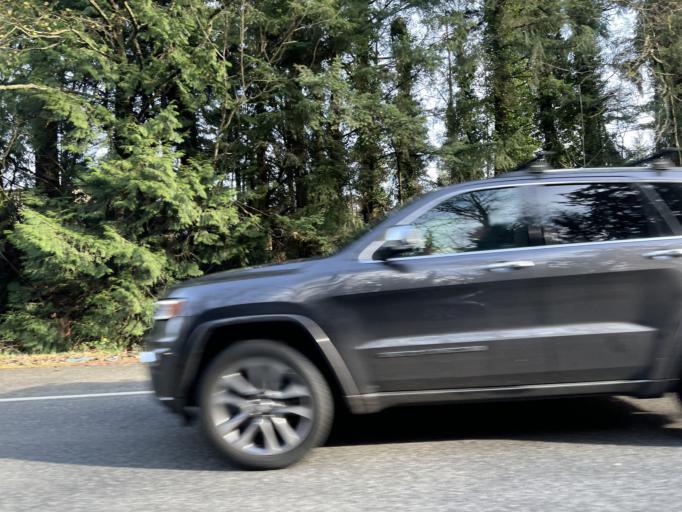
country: US
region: Washington
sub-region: Kitsap County
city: Bainbridge Island
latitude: 47.6385
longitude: -122.5128
